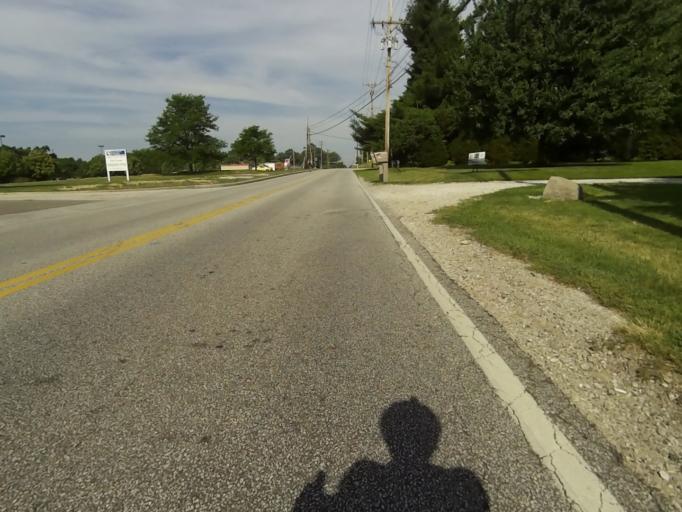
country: US
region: Ohio
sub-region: Summit County
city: Hudson
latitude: 41.2030
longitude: -81.4369
